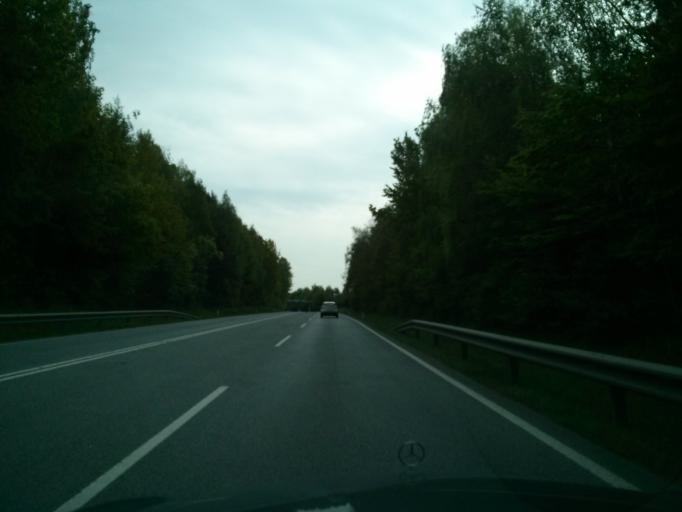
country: AT
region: Burgenland
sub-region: Politischer Bezirk Oberwart
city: Markt Allhau
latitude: 47.2772
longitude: 16.1059
